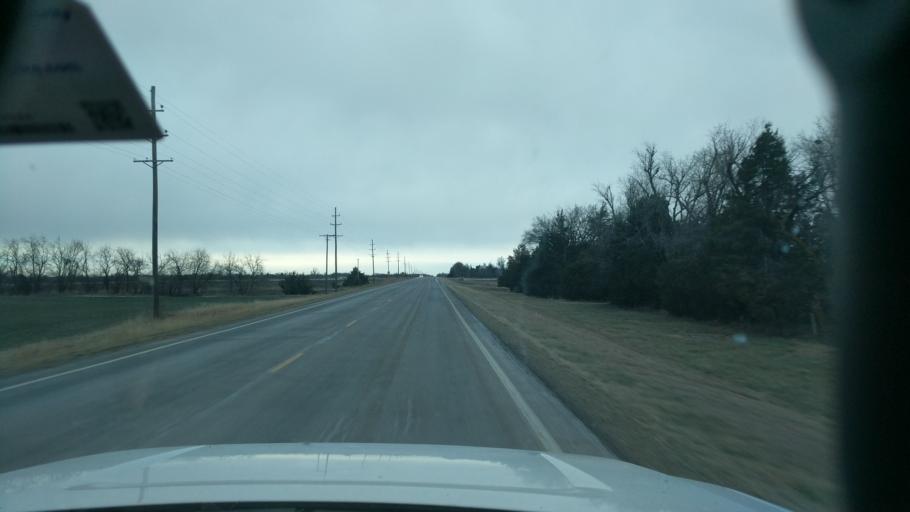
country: US
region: Kansas
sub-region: Marion County
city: Hillsboro
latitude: 38.2936
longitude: -97.3347
